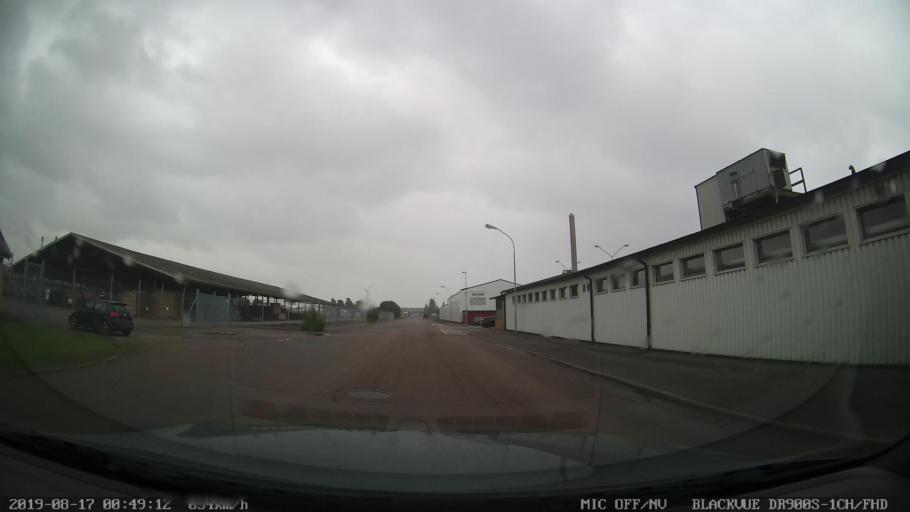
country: SE
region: Skane
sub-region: Landskrona
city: Landskrona
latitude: 55.8658
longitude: 12.8435
